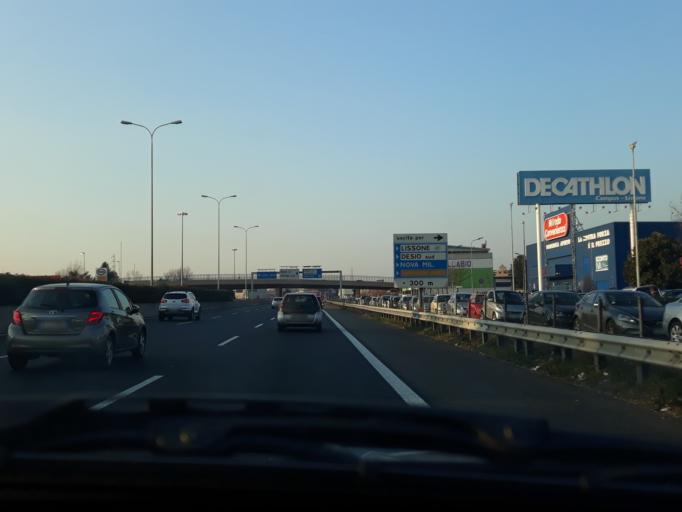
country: IT
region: Lombardy
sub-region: Provincia di Monza e Brianza
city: Lissone
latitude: 45.6046
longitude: 9.2286
